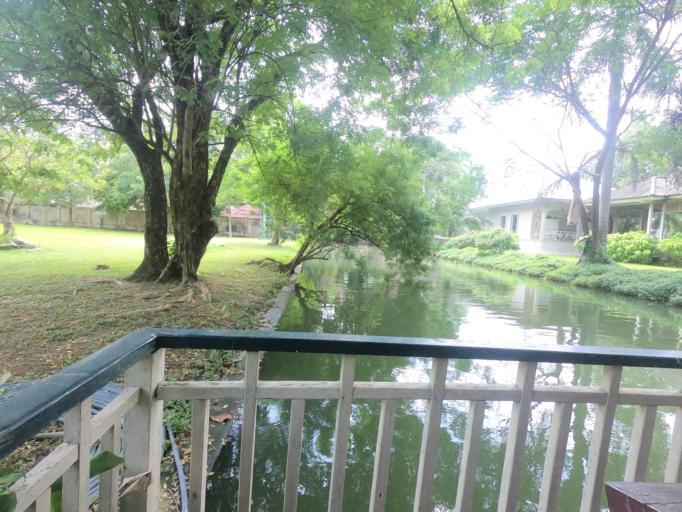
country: TH
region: Nakhon Pathom
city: Nakhon Pathom
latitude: 13.8185
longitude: 100.0447
